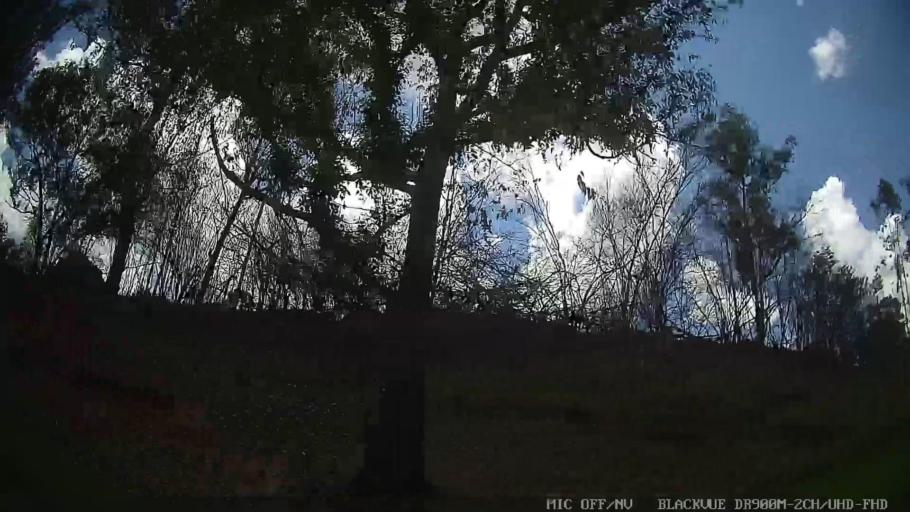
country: BR
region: Sao Paulo
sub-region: Serra Negra
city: Serra Negra
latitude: -22.6484
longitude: -46.7389
